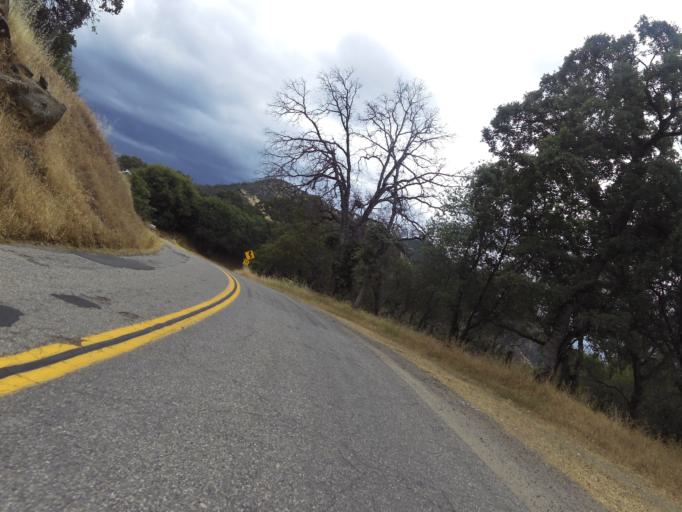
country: US
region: California
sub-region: Madera County
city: Ahwahnee
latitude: 37.3461
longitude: -119.7652
